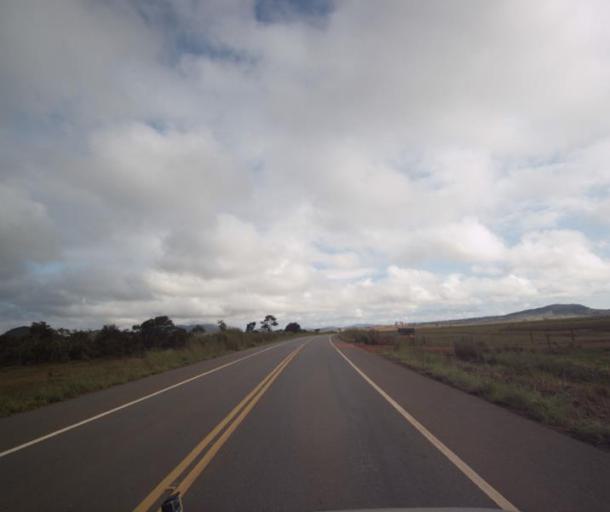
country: BR
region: Goias
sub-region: Barro Alto
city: Barro Alto
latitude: -15.2926
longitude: -48.6771
